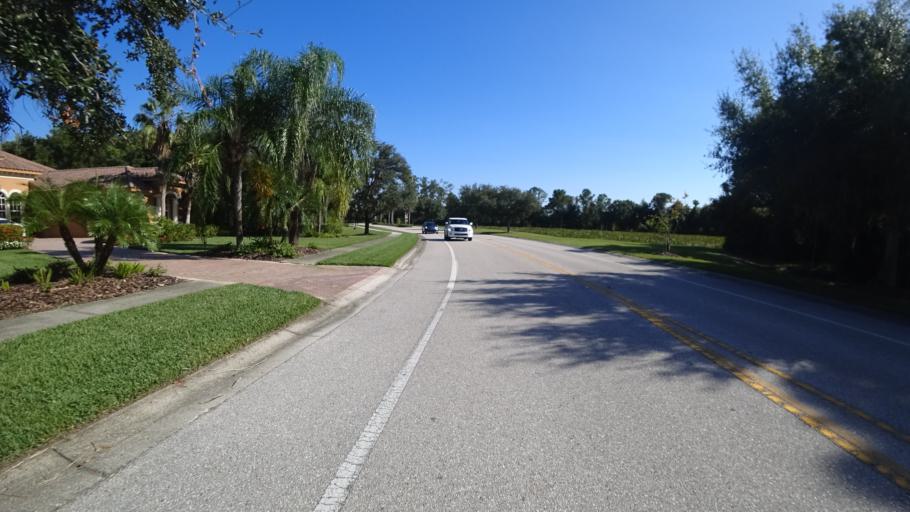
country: US
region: Florida
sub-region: Sarasota County
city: The Meadows
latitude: 27.4041
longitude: -82.4364
